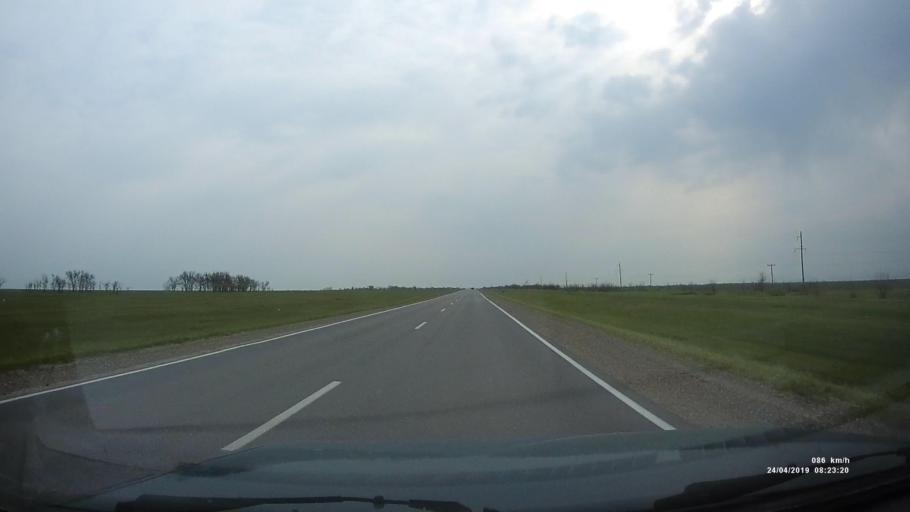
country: RU
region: Kalmykiya
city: Priyutnoye
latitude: 46.1169
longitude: 43.7348
